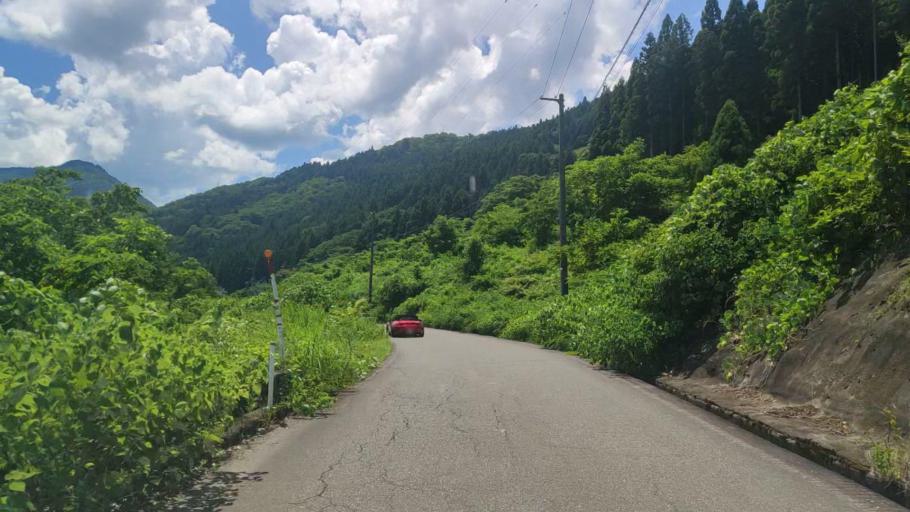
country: JP
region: Fukui
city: Ono
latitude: 35.8874
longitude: 136.5058
